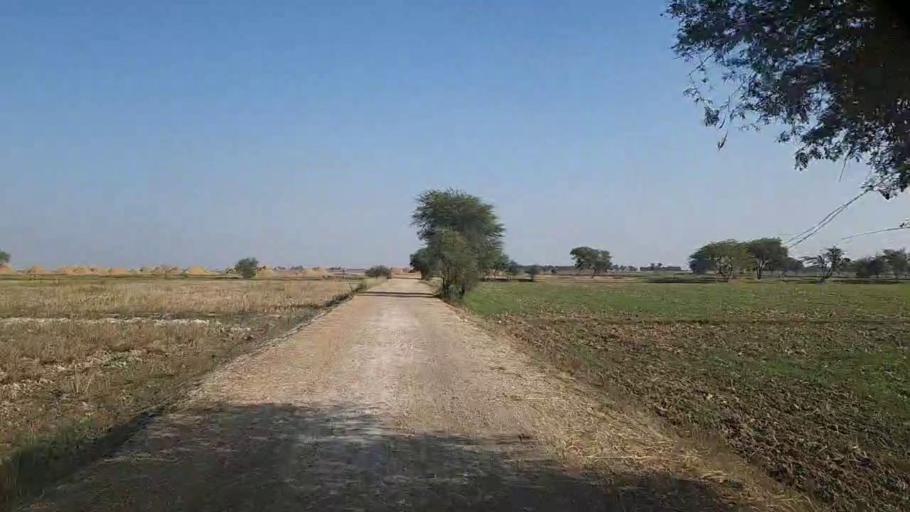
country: PK
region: Sindh
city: Thul
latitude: 28.3593
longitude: 68.7672
